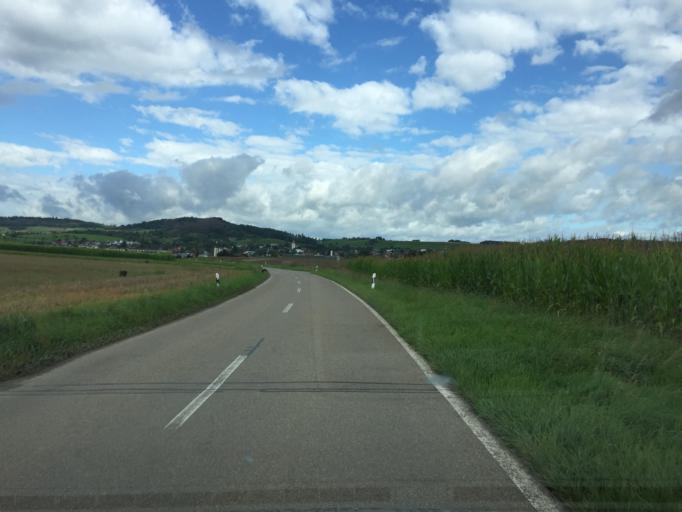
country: CH
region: Schaffhausen
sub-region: Bezirk Unterklettgau
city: Wilchingen
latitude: 47.6560
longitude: 8.4407
